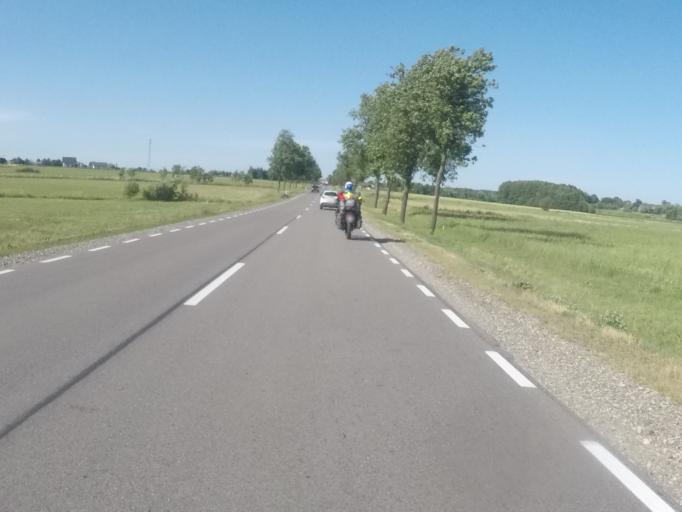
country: PL
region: Podlasie
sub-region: Powiat bialostocki
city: Zabludow
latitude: 53.0039
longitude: 23.3303
